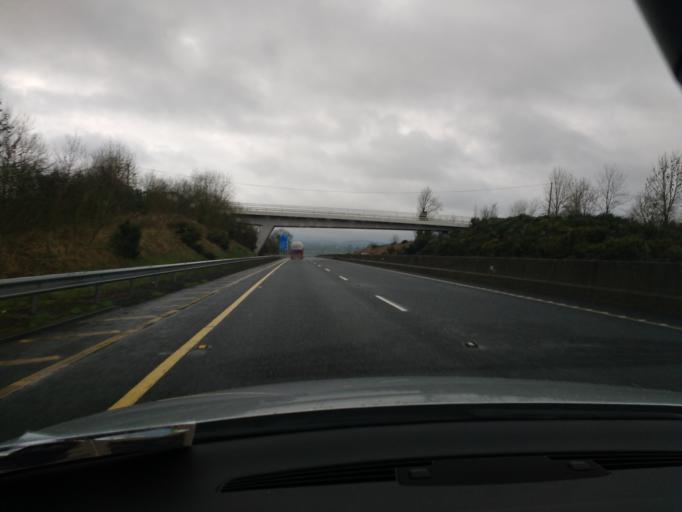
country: IE
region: Munster
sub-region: North Tipperary
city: Nenagh
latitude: 52.8443
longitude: -8.2250
